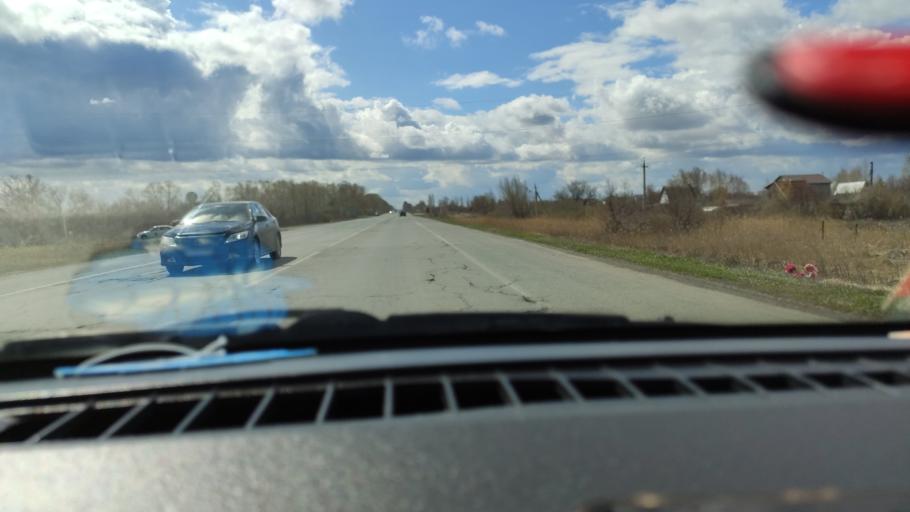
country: RU
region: Samara
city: Tol'yatti
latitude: 53.7063
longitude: 49.4222
